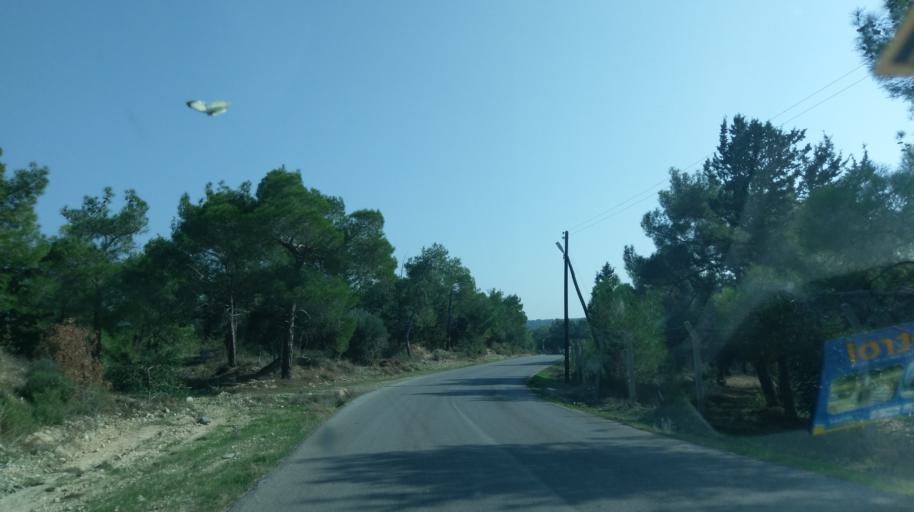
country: CY
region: Keryneia
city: Lapithos
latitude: 35.3274
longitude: 33.0418
